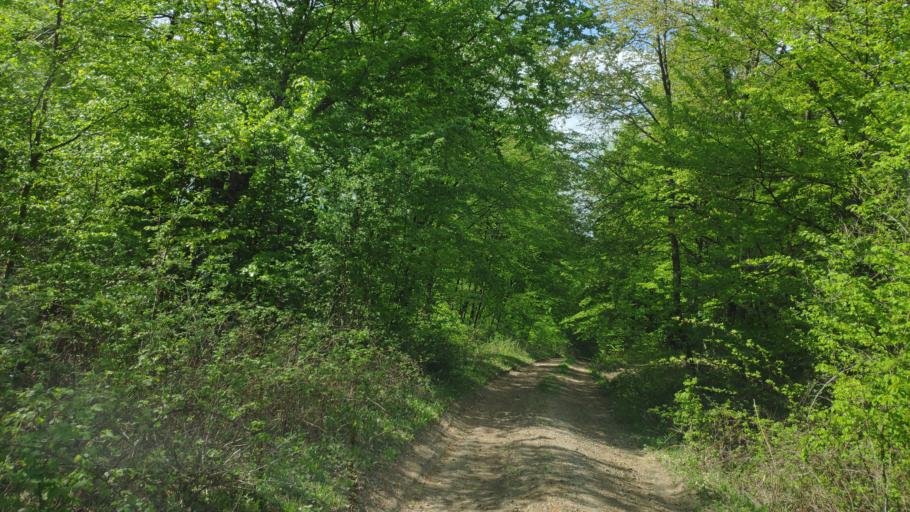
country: SK
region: Kosicky
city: Kosice
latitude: 48.6734
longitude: 21.4494
